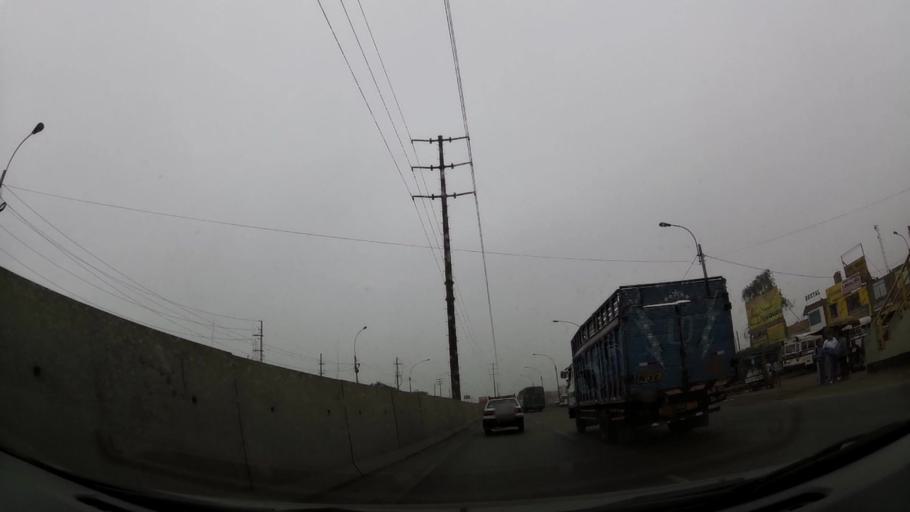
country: PE
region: Lima
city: Ventanilla
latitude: -11.8404
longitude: -77.1049
